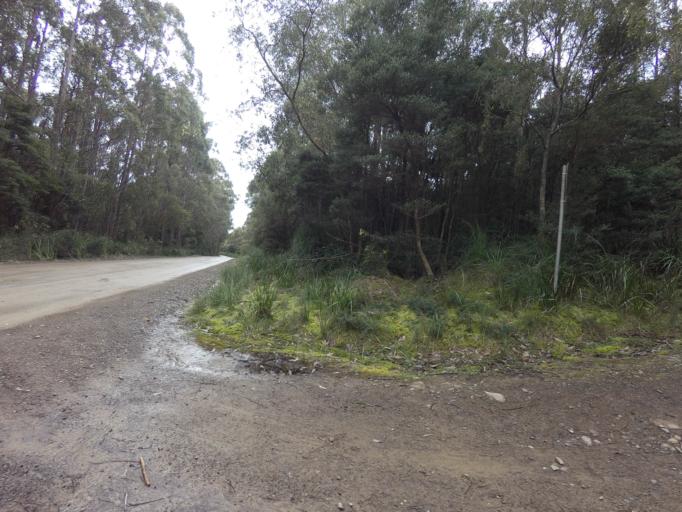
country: AU
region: Tasmania
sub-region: Huon Valley
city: Geeveston
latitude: -43.4554
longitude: 146.9039
